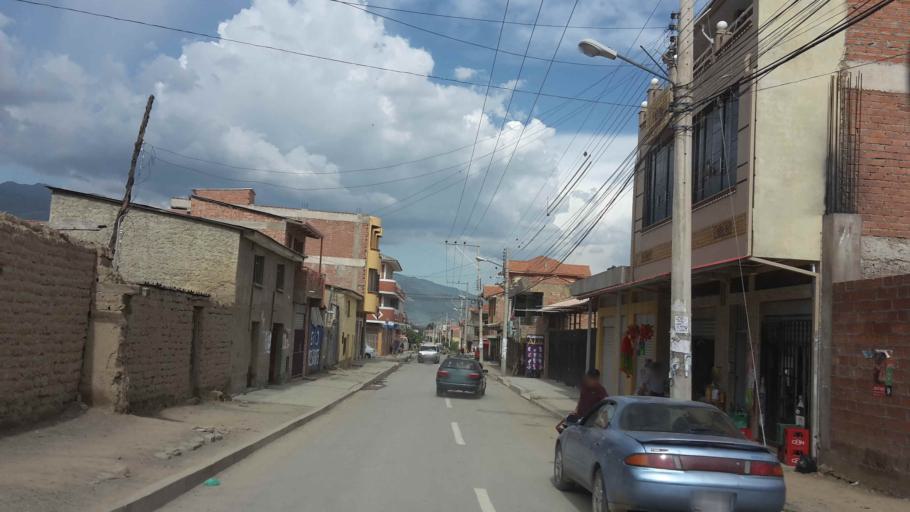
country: BO
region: Cochabamba
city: Cochabamba
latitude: -17.3385
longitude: -66.2646
